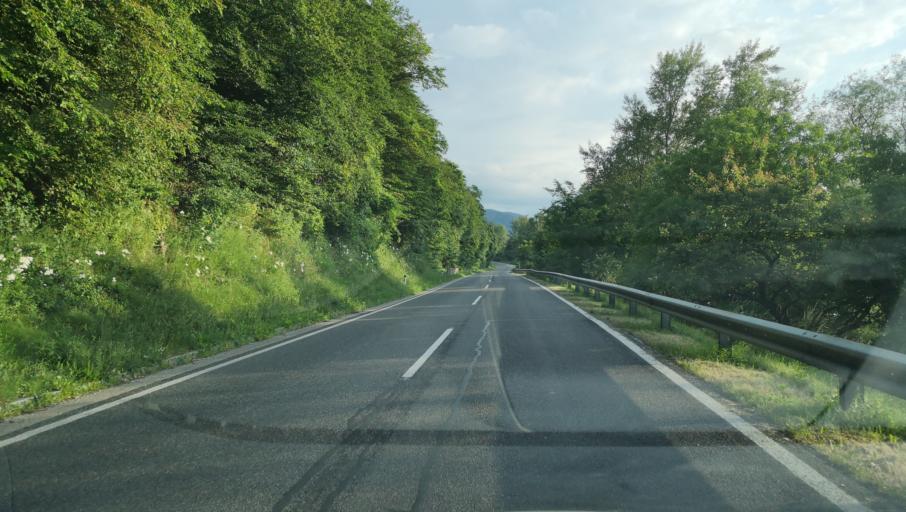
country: AT
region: Lower Austria
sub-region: Politischer Bezirk Krems
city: Durnstein
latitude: 48.3904
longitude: 15.4725
